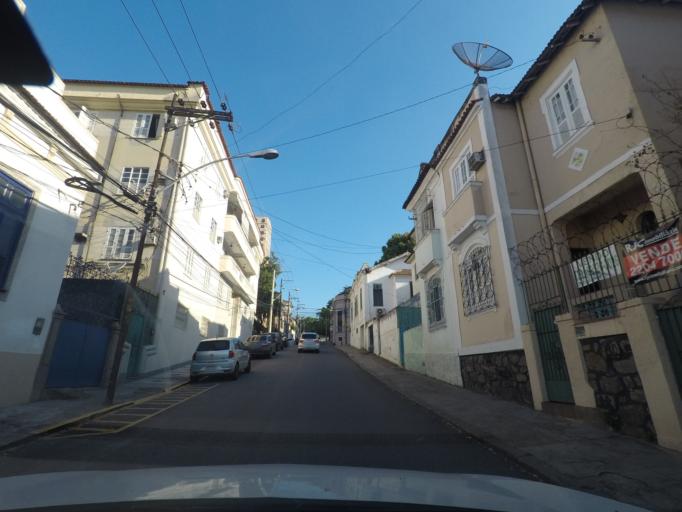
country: BR
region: Rio de Janeiro
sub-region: Rio De Janeiro
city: Rio de Janeiro
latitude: -22.9014
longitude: -43.2242
